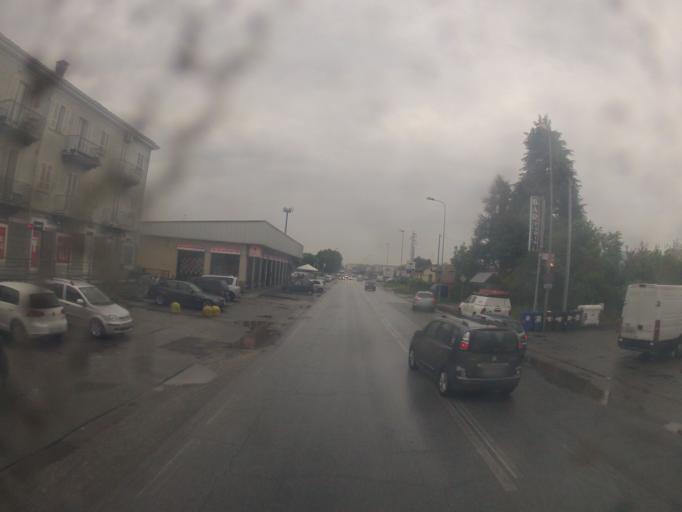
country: IT
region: Piedmont
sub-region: Provincia di Torino
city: Tagliaferro
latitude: 44.9915
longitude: 7.6713
